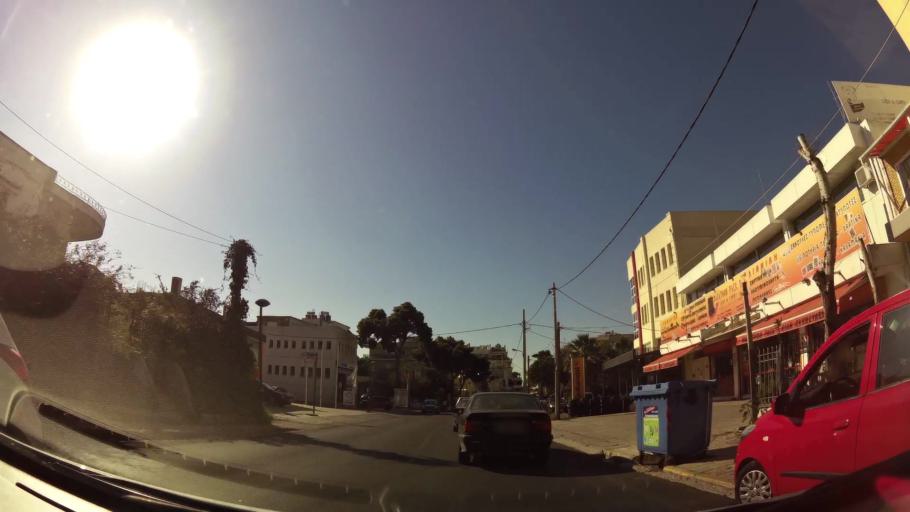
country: GR
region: Attica
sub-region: Nomarchia Athinas
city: Metamorfosi
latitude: 38.0657
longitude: 23.7656
